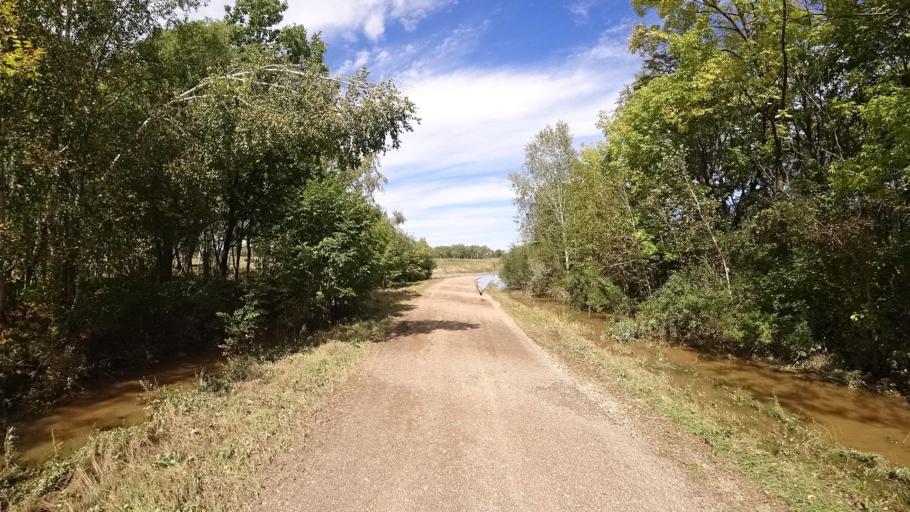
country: RU
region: Primorskiy
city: Yakovlevka
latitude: 44.6647
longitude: 133.7508
